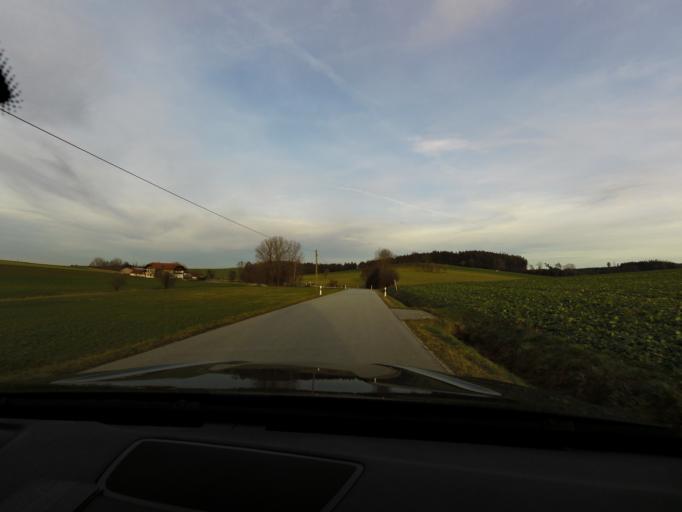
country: DE
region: Bavaria
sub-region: Lower Bavaria
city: Vilsheim
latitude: 48.4350
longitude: 12.1272
